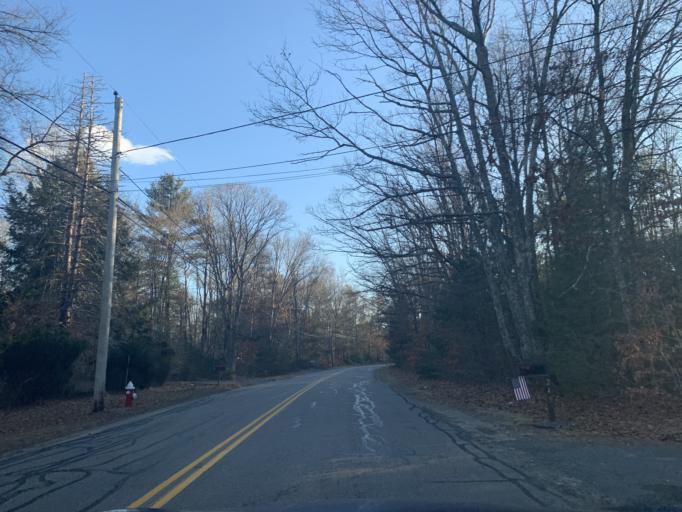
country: US
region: Massachusetts
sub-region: Bristol County
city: Norton
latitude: 41.9132
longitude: -71.2030
